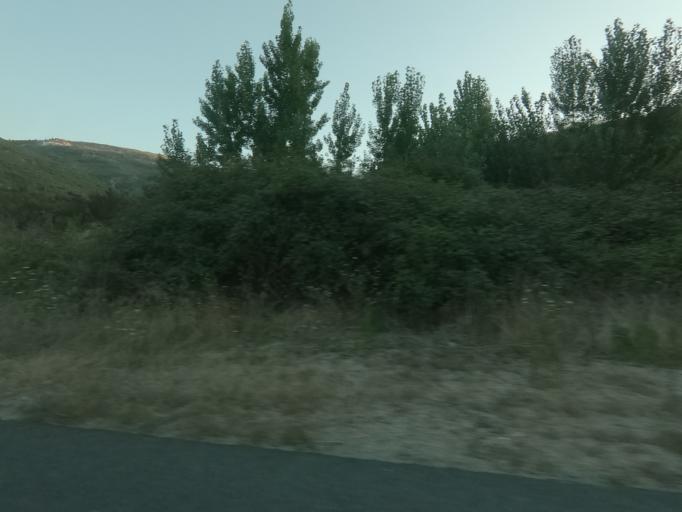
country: PT
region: Vila Real
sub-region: Peso da Regua
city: Peso da Regua
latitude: 41.1479
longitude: -7.7328
